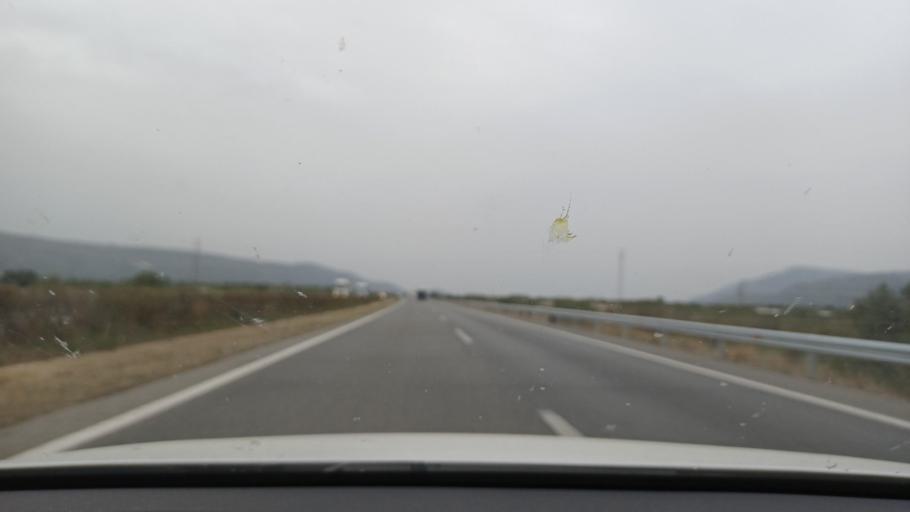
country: ES
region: Catalonia
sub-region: Provincia de Tarragona
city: Ulldecona
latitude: 40.6000
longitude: 0.4717
